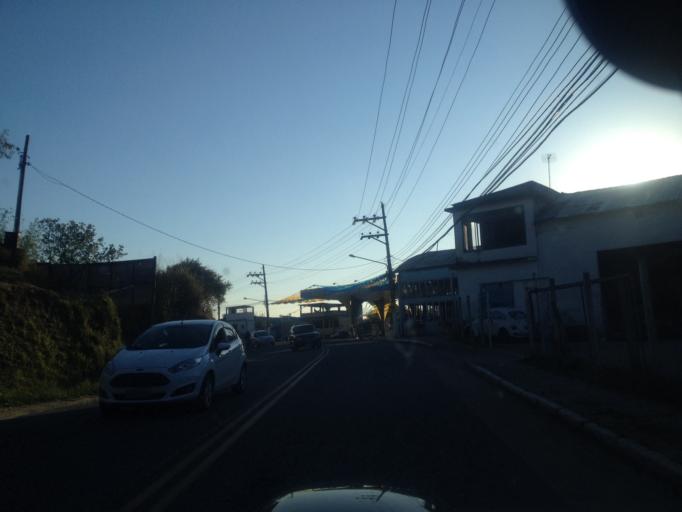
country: BR
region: Rio de Janeiro
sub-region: Quatis
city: Quatis
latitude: -22.4146
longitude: -44.2726
